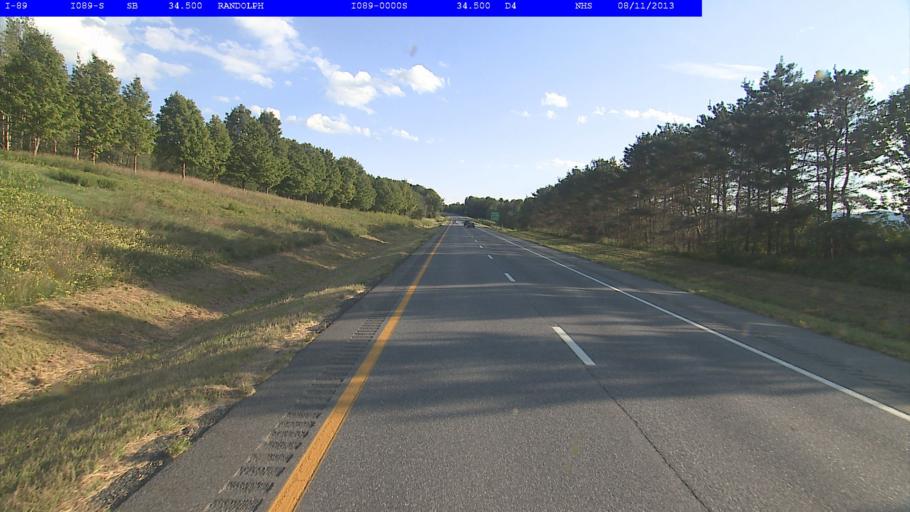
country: US
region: Vermont
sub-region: Orange County
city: Randolph
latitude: 43.9968
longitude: -72.6250
